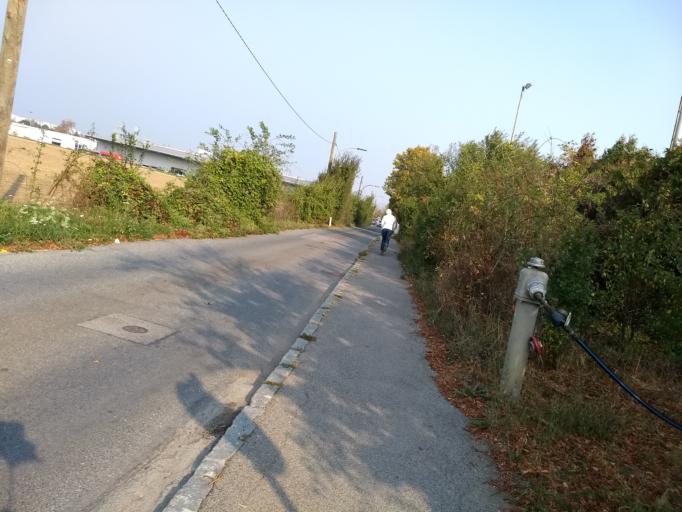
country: AT
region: Lower Austria
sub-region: Politischer Bezirk Modling
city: Brunn am Gebirge
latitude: 48.1210
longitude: 16.2896
